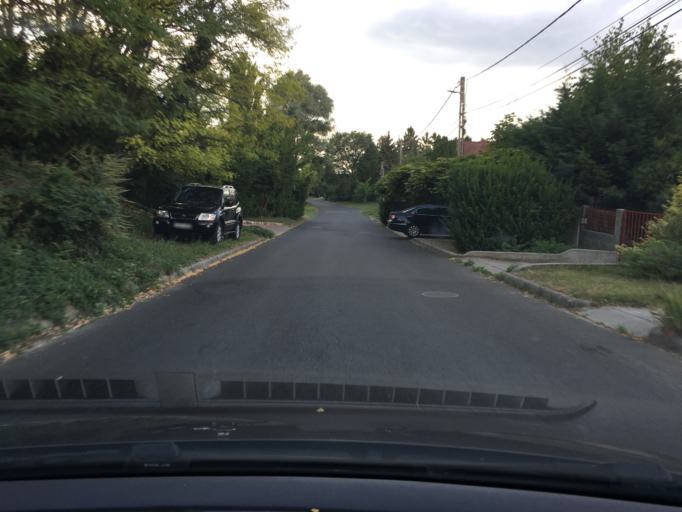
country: HU
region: Pest
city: Veresegyhaz
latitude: 47.6449
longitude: 19.3045
